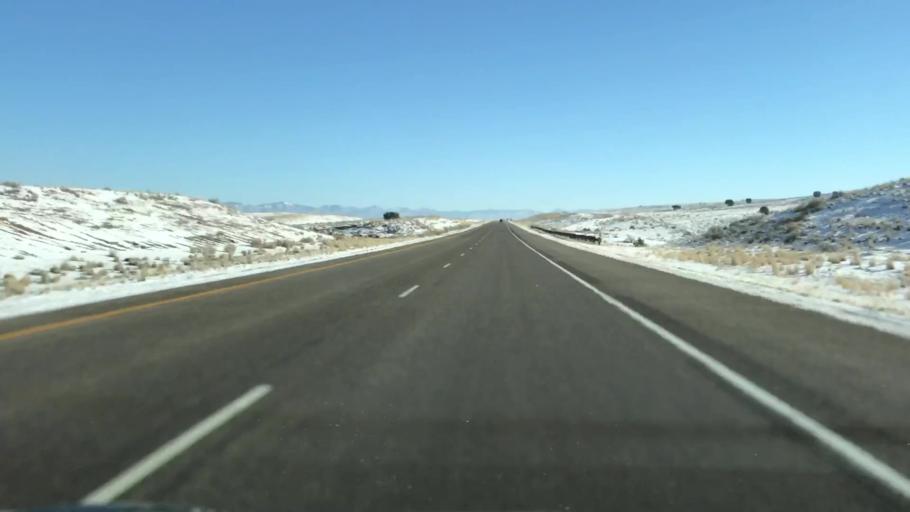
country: US
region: Colorado
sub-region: Mesa County
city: Loma
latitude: 39.2225
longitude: -108.9430
